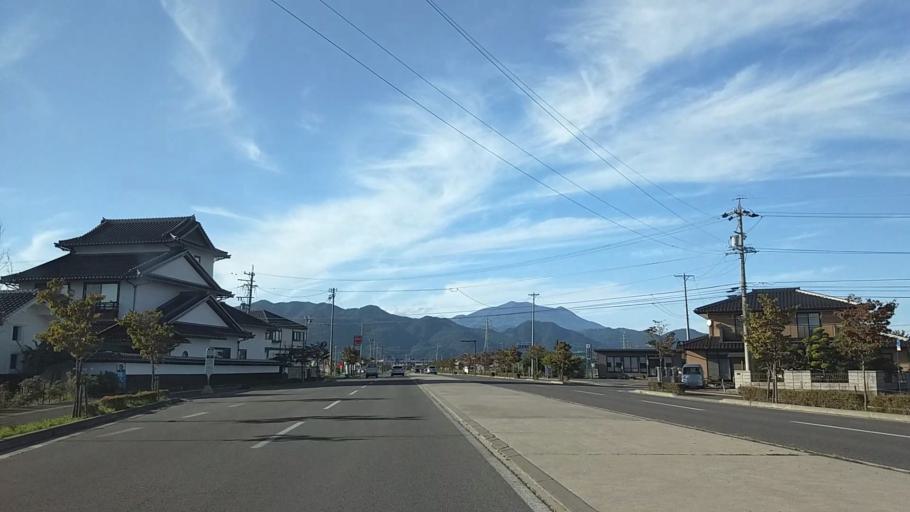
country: JP
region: Nagano
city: Nagano-shi
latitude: 36.5976
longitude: 138.1820
